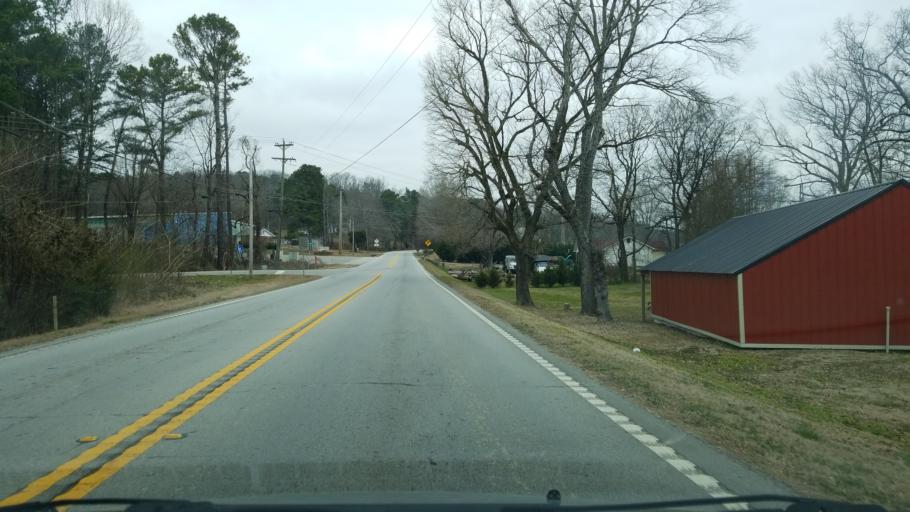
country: US
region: Georgia
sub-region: Catoosa County
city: Indian Springs
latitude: 34.9684
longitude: -85.1824
